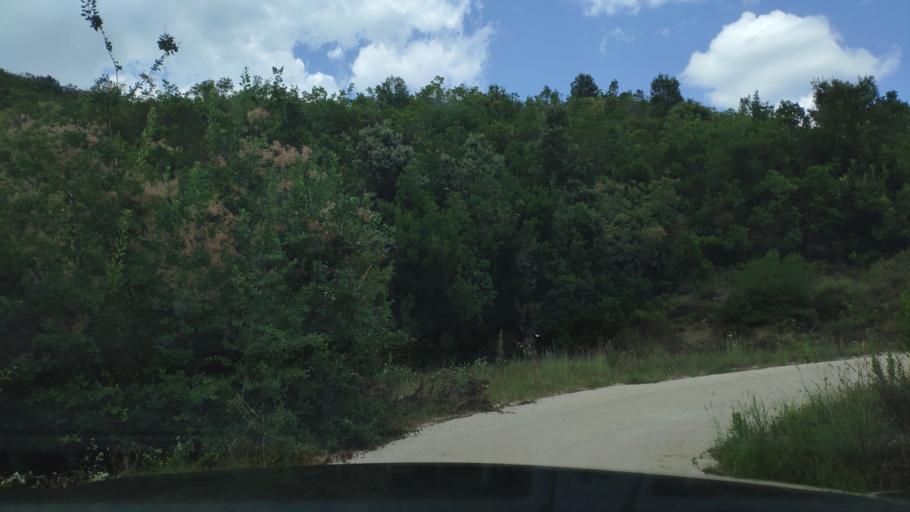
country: GR
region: Epirus
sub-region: Nomos Artas
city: Agios Dimitrios
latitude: 39.3122
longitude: 21.0178
